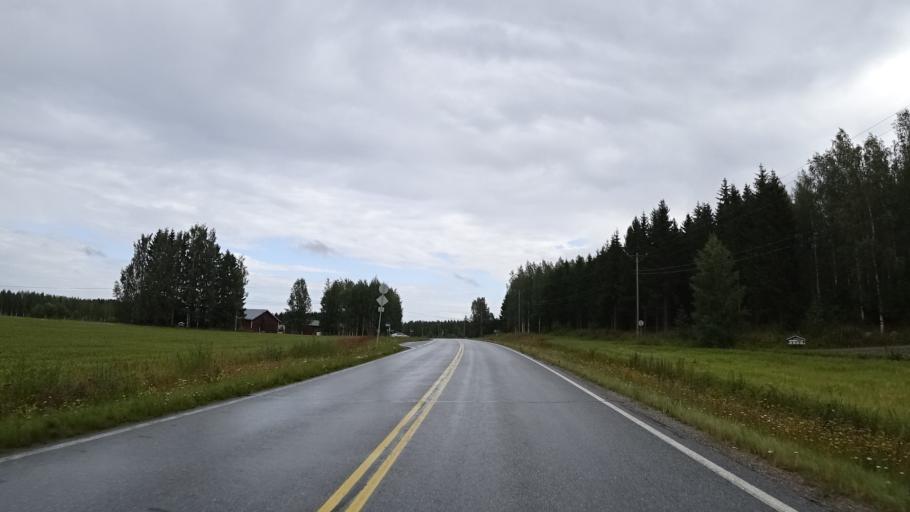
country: FI
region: North Karelia
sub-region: Keski-Karjala
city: Raeaekkylae
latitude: 62.0381
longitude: 29.5415
